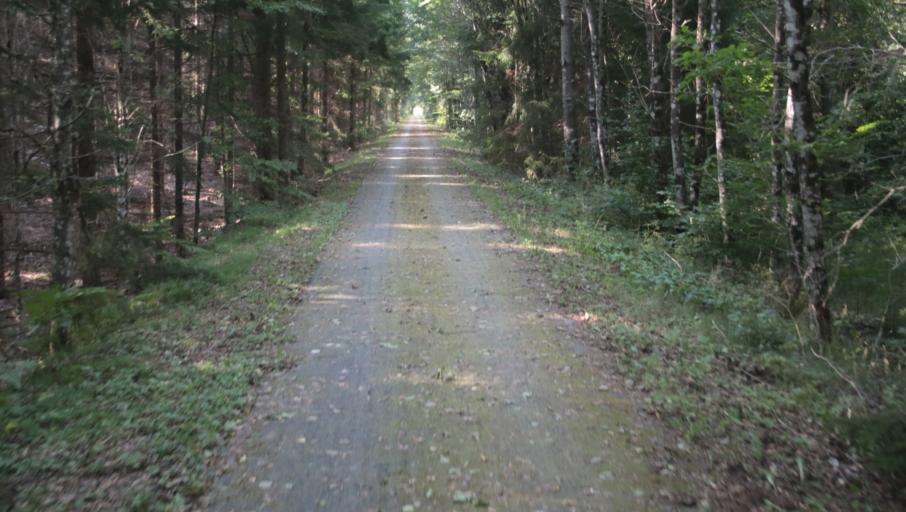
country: SE
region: Blekinge
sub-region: Karlshamns Kommun
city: Svangsta
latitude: 56.3136
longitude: 14.7138
